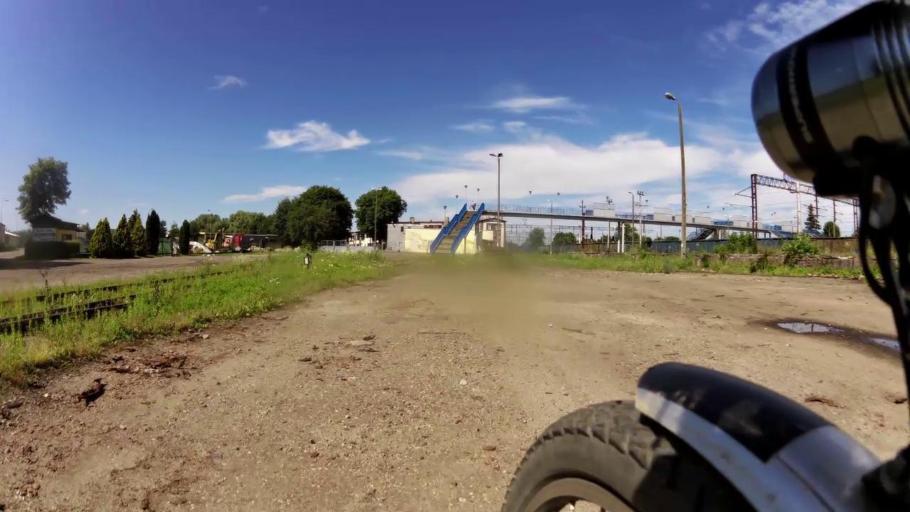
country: PL
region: West Pomeranian Voivodeship
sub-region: Powiat bialogardzki
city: Bialogard
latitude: 54.0109
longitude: 15.9767
